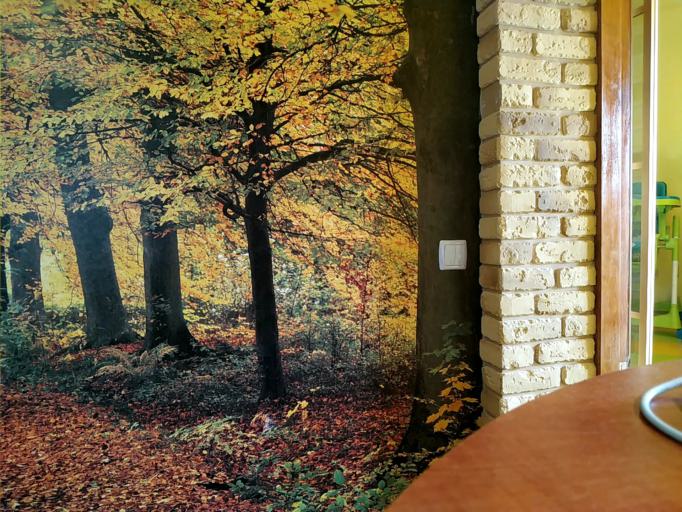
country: RU
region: Tverskaya
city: Kalashnikovo
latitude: 57.3341
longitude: 35.3328
